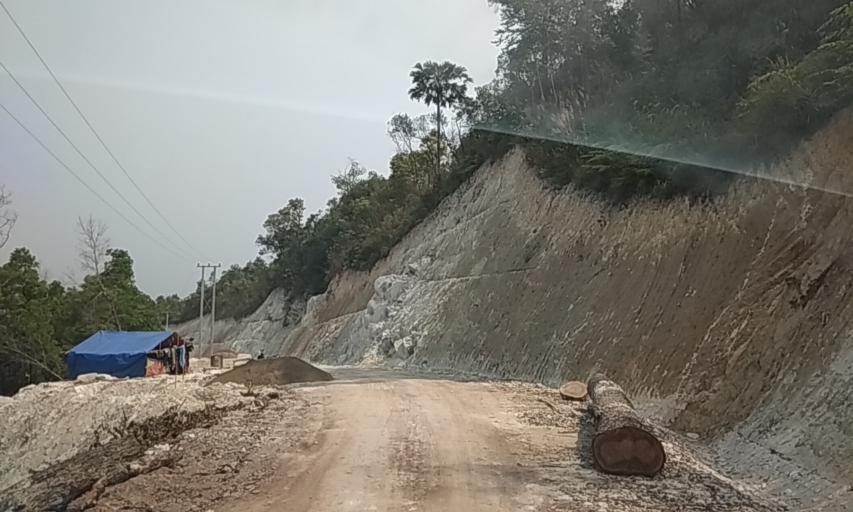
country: VN
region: Huyen Dien Bien
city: Dien Bien Phu
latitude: 21.4879
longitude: 102.7848
